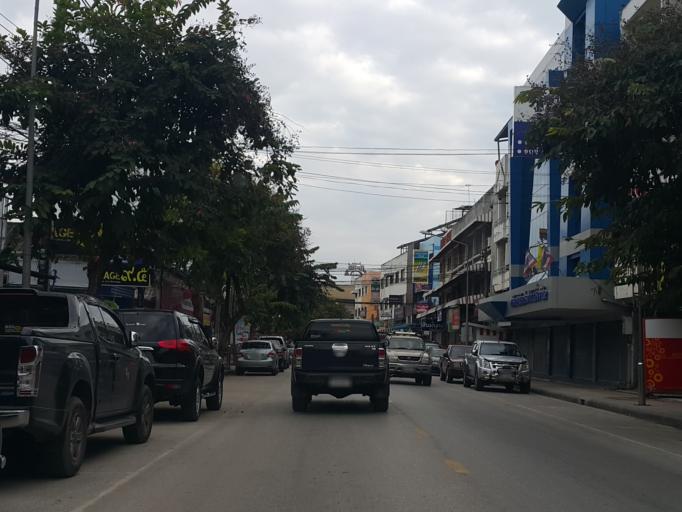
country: TH
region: Lampang
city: Lampang
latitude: 18.2879
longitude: 99.4853
